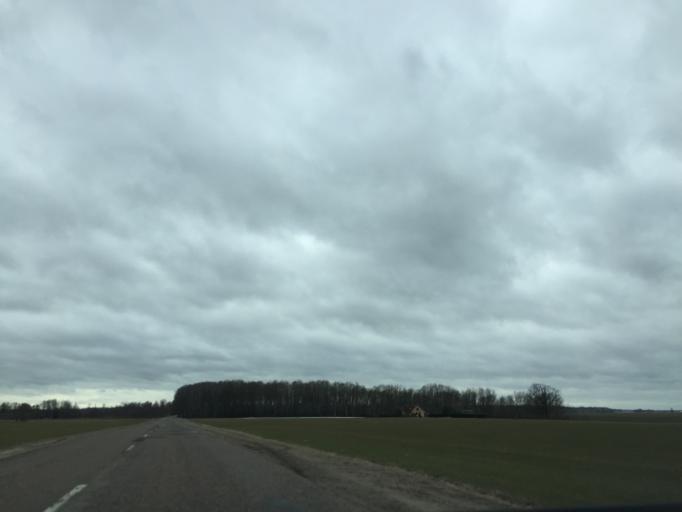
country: LV
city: Tervete
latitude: 56.5224
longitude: 23.4971
